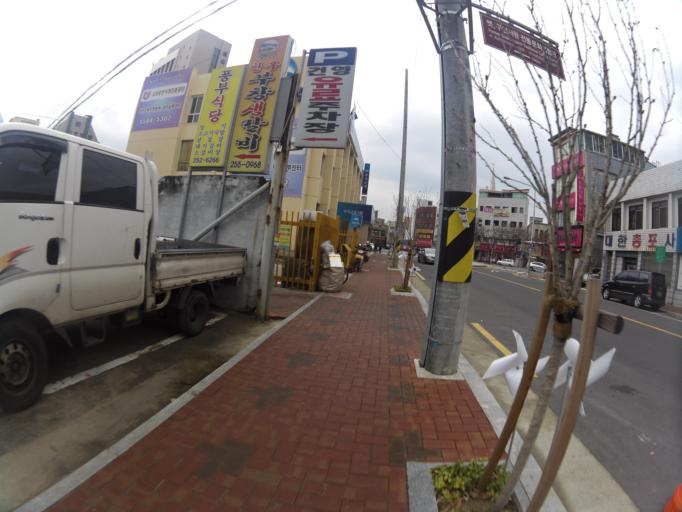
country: KR
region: Daegu
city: Daegu
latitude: 35.8699
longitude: 128.5853
